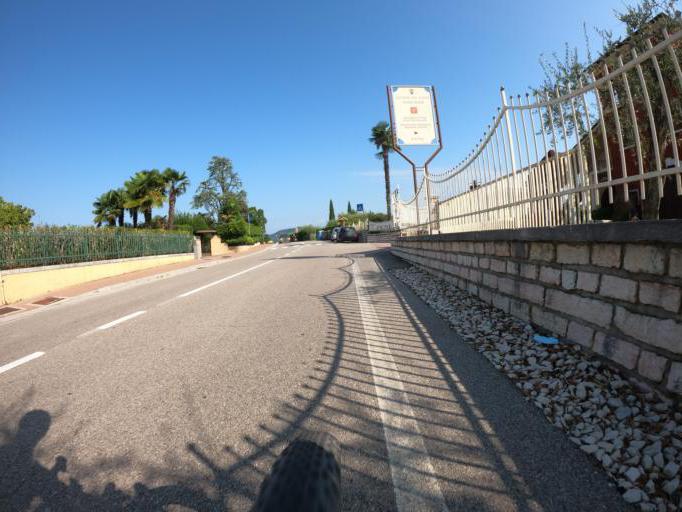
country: IT
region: Veneto
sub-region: Provincia di Verona
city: Bardolino
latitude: 45.5391
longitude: 10.7345
